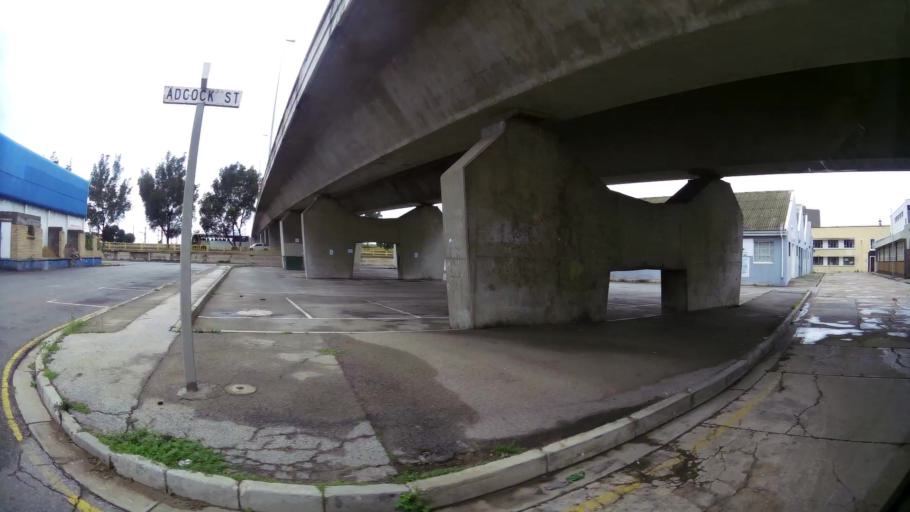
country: ZA
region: Eastern Cape
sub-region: Nelson Mandela Bay Metropolitan Municipality
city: Port Elizabeth
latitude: -33.9503
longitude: 25.6107
